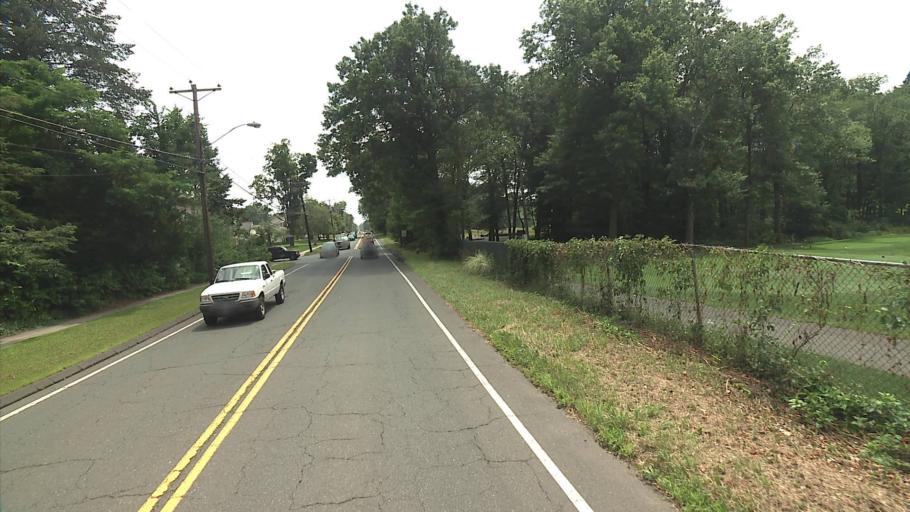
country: US
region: Connecticut
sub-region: Hartford County
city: Newington
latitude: 41.6904
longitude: -72.7320
